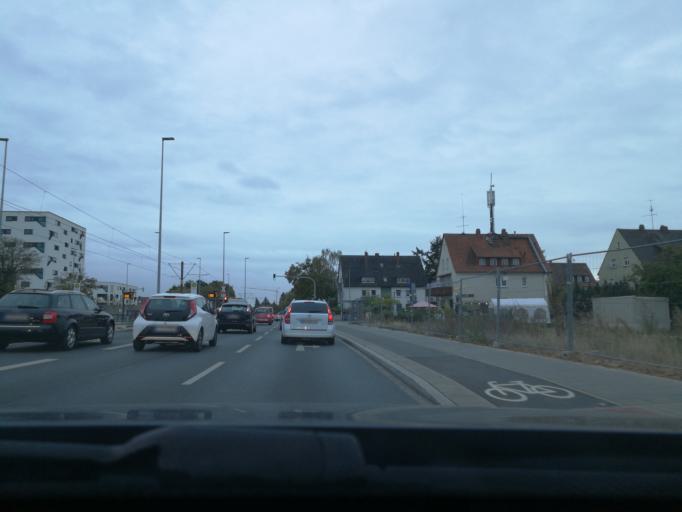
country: DE
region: Bavaria
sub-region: Regierungsbezirk Mittelfranken
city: Wetzendorf
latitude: 49.4808
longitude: 11.0603
